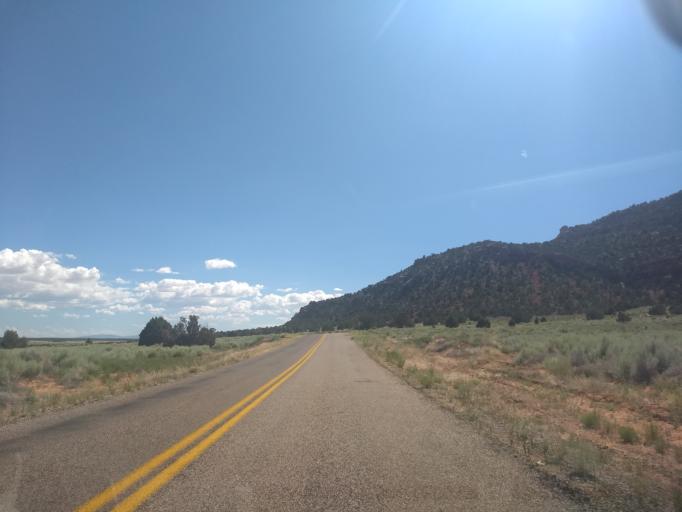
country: US
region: Utah
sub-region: Washington County
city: Hildale
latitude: 36.9638
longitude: -112.8721
